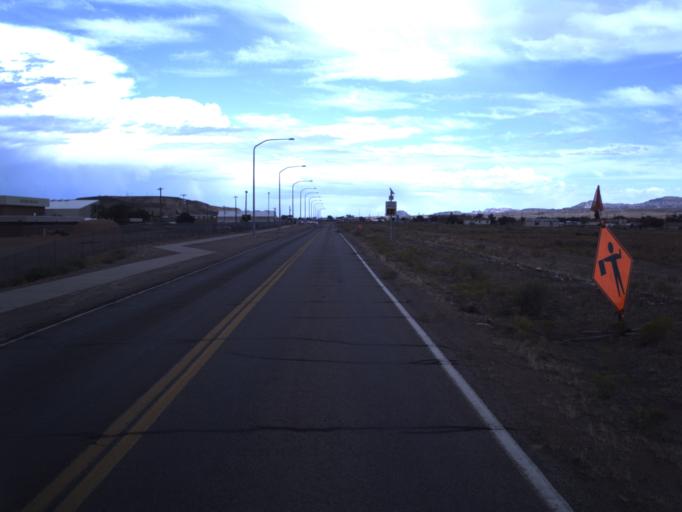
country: US
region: Utah
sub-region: San Juan County
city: Blanding
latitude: 37.2670
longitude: -109.3151
